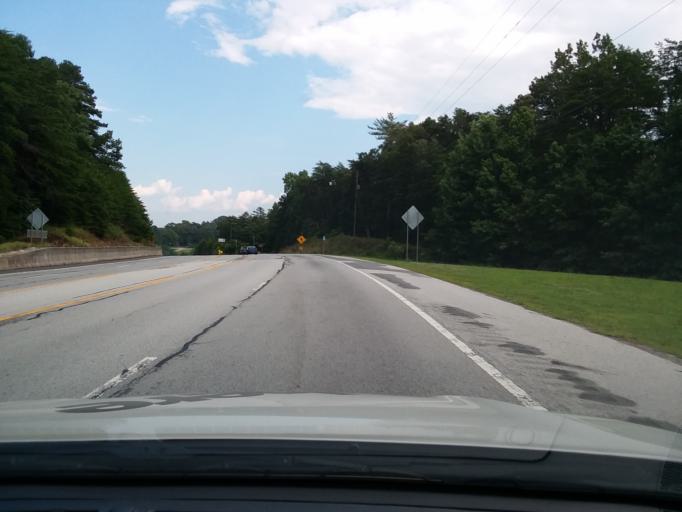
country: US
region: Georgia
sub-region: Rabun County
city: Clayton
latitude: 34.7410
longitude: -83.3994
